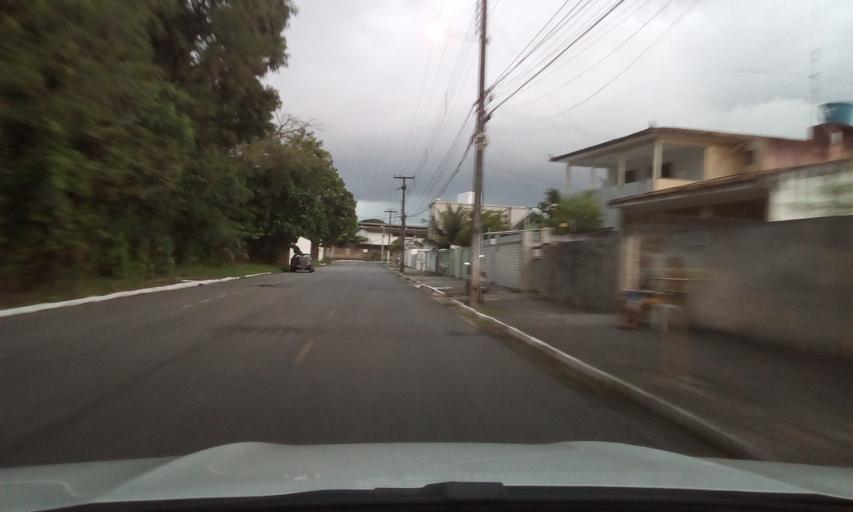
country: BR
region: Paraiba
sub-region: Joao Pessoa
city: Joao Pessoa
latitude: -7.1621
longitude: -34.8639
